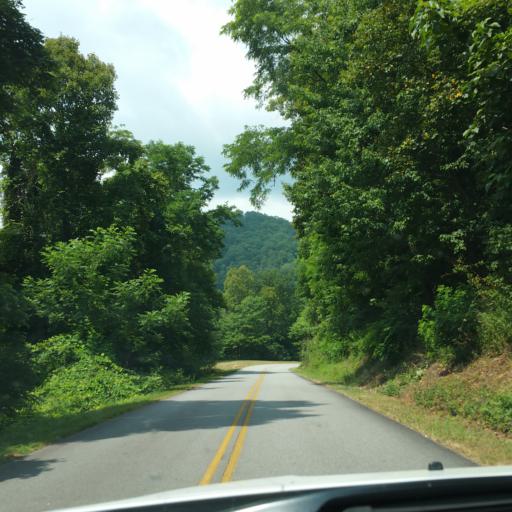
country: US
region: North Carolina
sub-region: Buncombe County
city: Bent Creek
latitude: 35.4744
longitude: -82.6170
